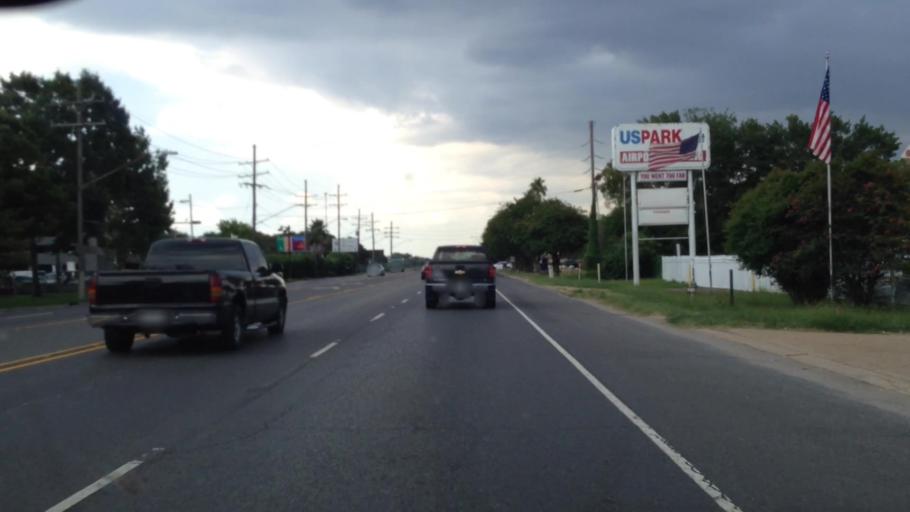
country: US
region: Louisiana
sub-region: Jefferson Parish
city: Kenner
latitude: 29.9827
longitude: -90.2596
